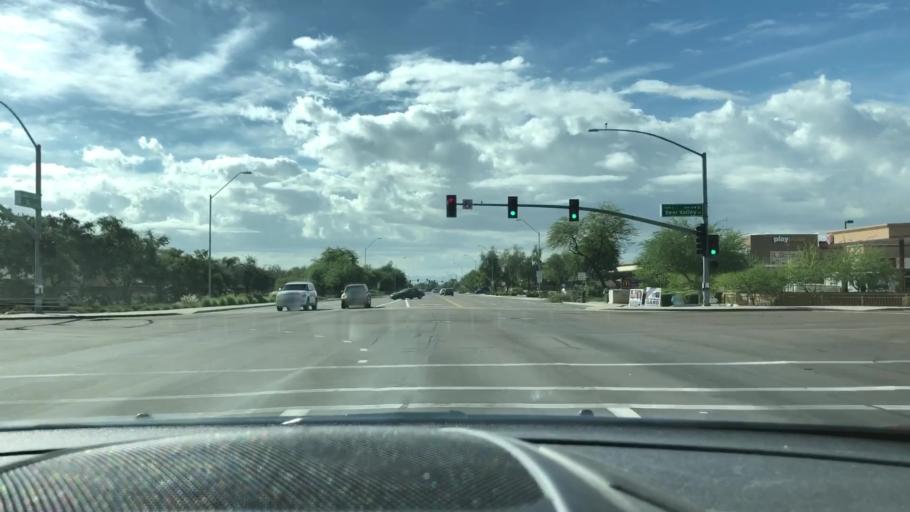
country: US
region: Arizona
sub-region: Maricopa County
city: Sun City
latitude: 33.6818
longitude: -112.2378
